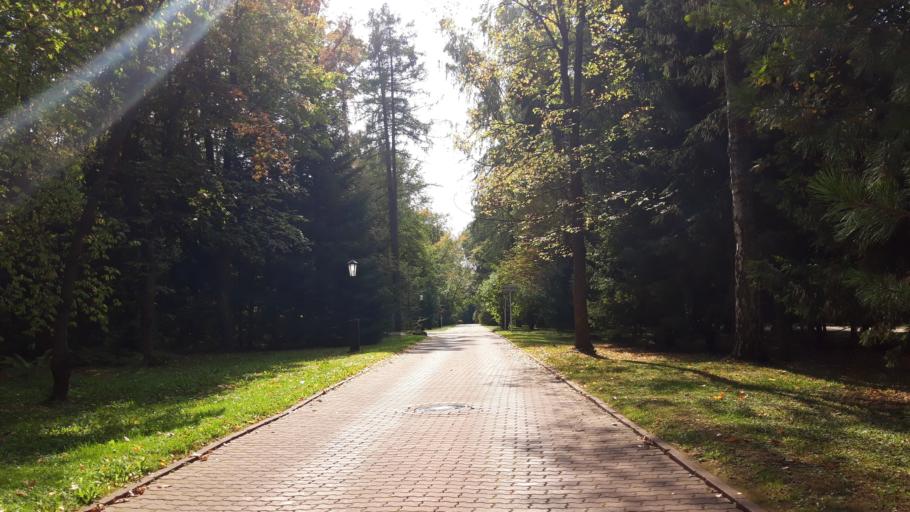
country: RU
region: Moskovskaya
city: Mendeleyevo
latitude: 56.0523
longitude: 37.2220
